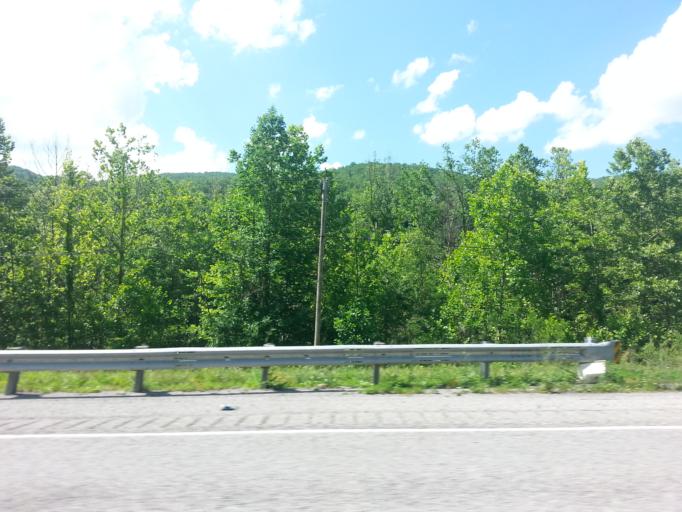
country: US
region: Kentucky
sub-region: Harlan County
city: Harlan
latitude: 36.9201
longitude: -83.1779
